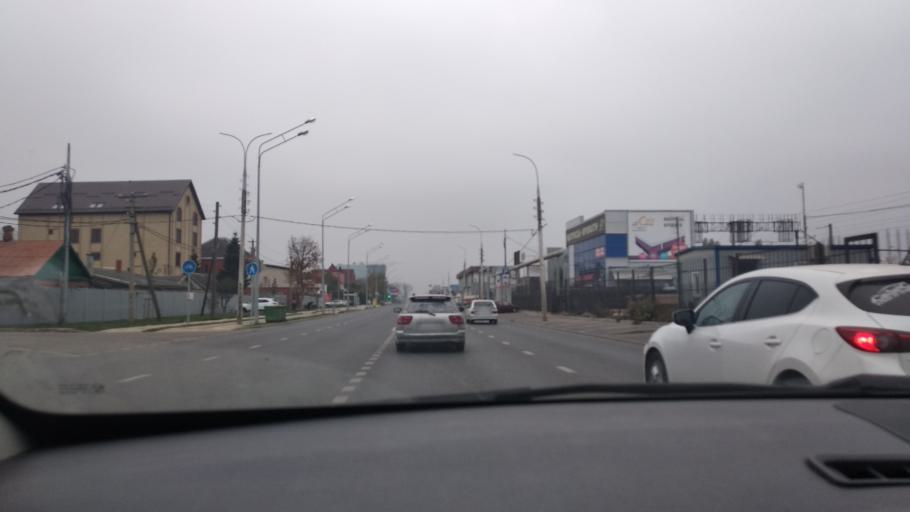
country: RU
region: Krasnodarskiy
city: Krasnodar
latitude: 45.0317
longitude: 39.0227
